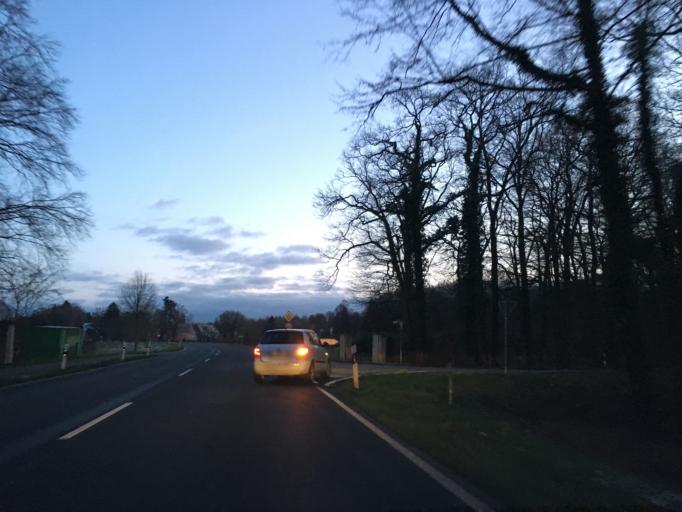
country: DE
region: North Rhine-Westphalia
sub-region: Regierungsbezirk Munster
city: Muenster
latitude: 51.8824
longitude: 7.6482
